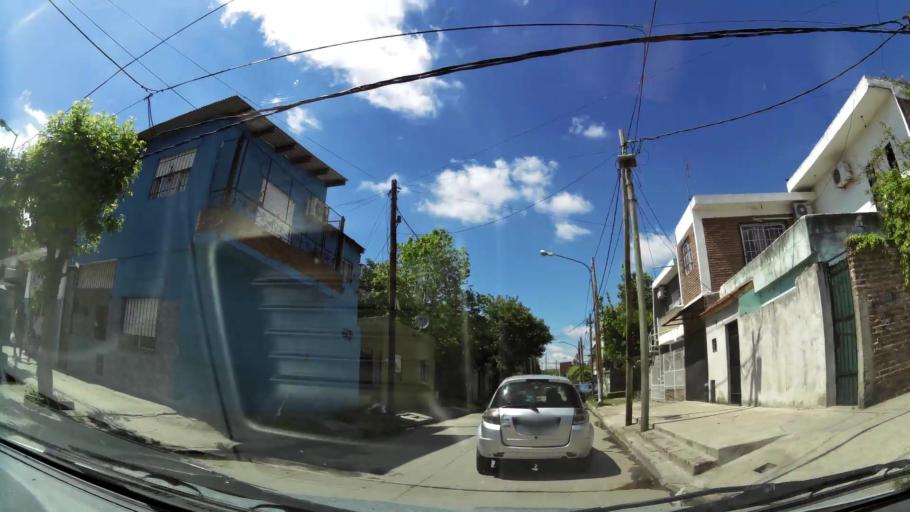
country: AR
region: Buenos Aires
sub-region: Partido de Lanus
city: Lanus
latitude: -34.6939
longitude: -58.4327
